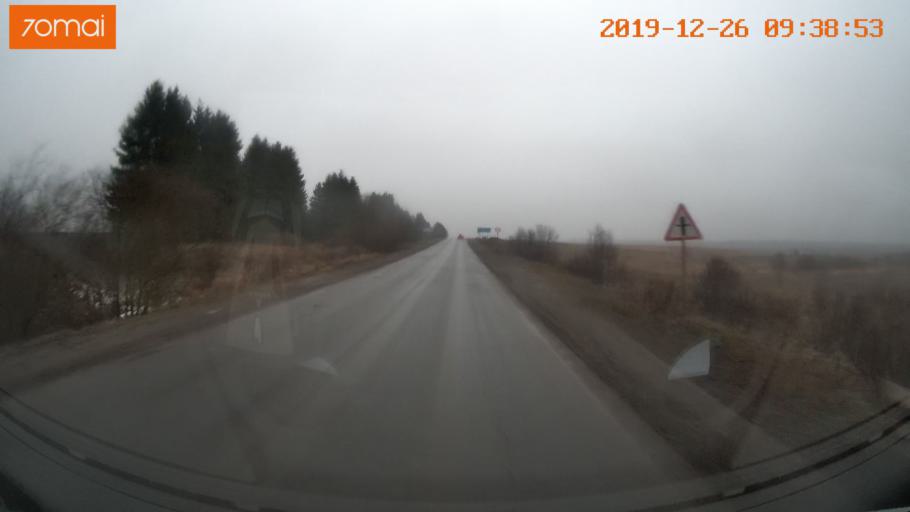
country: RU
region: Vologda
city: Vologda
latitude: 59.1489
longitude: 40.0345
